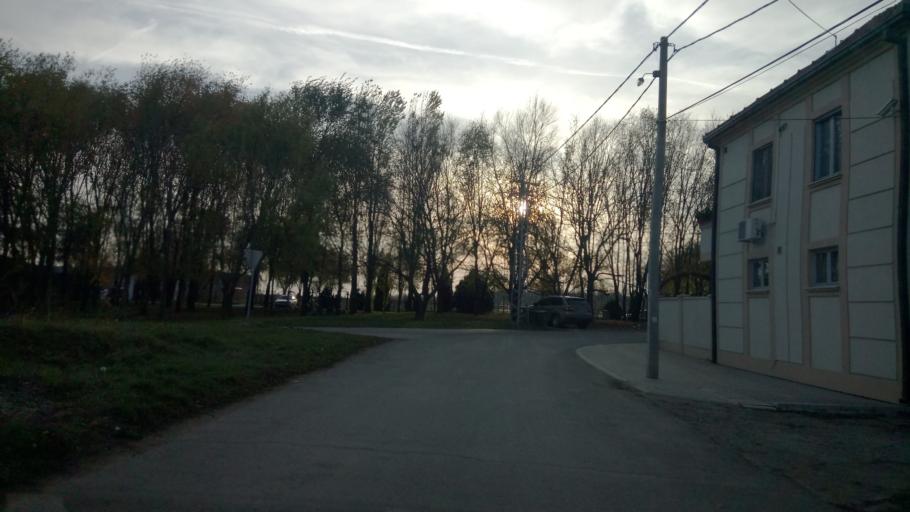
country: RS
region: Autonomna Pokrajina Vojvodina
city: Nova Pazova
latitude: 44.9357
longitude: 20.2161
